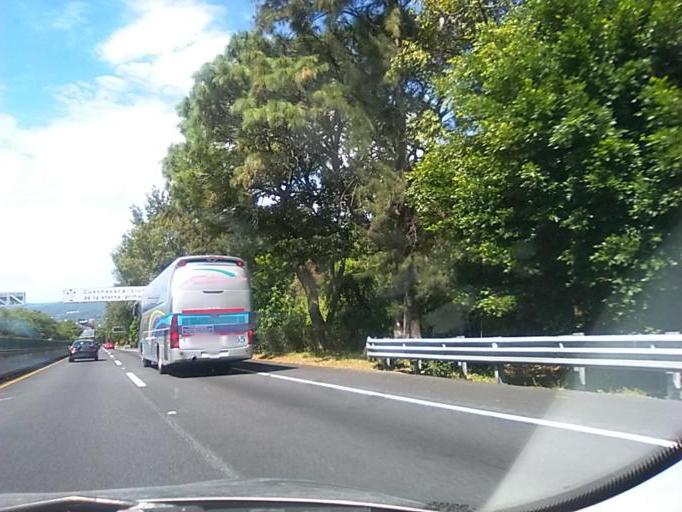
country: MX
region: Morelos
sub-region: Cuernavaca
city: Lomas de Ahuatepec
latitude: 18.9823
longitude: -99.2186
